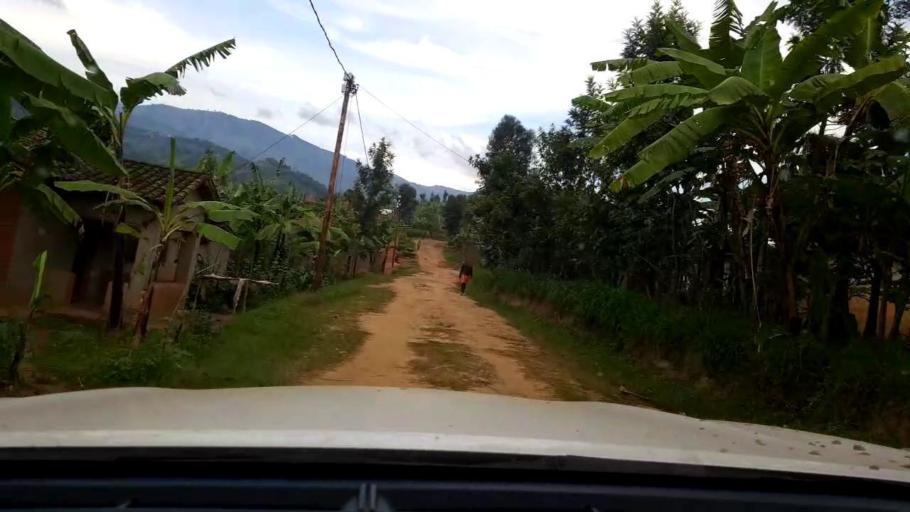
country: RW
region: Western Province
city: Kibuye
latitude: -2.0049
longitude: 29.3728
